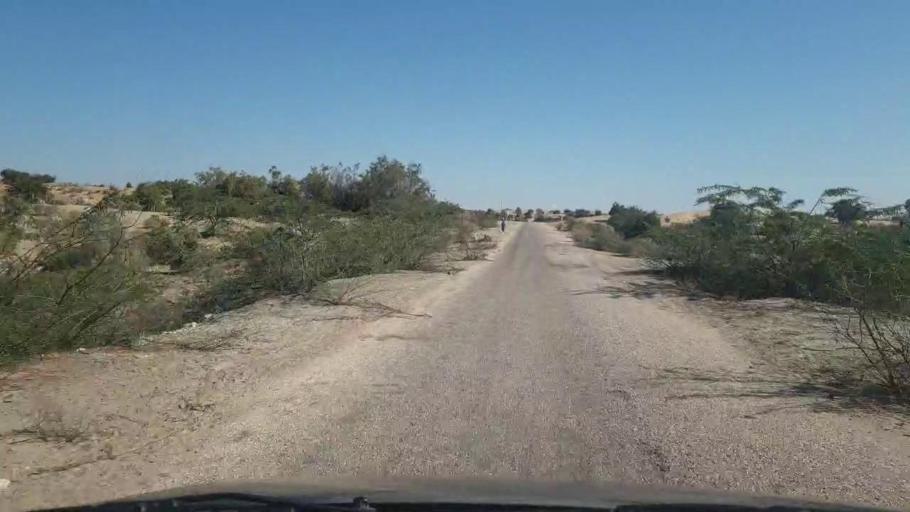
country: PK
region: Sindh
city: Bozdar
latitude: 27.0063
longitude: 68.9037
